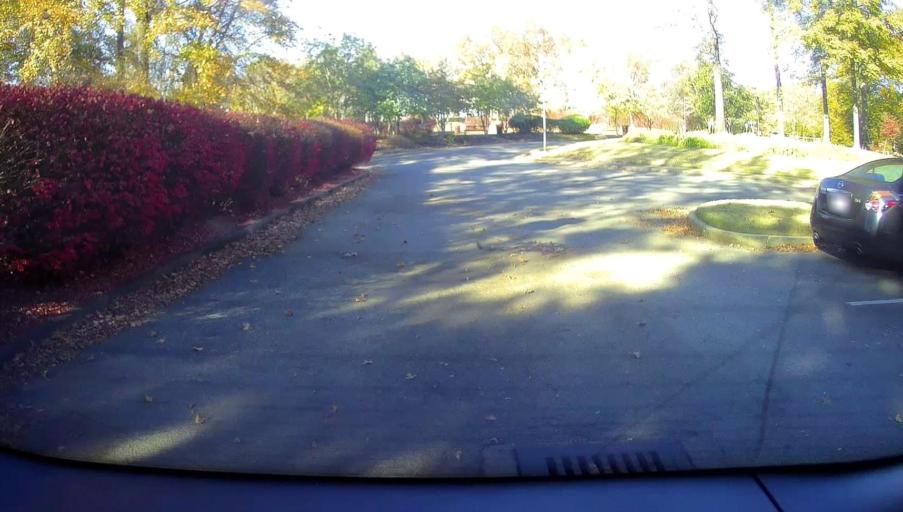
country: US
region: Tennessee
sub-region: Shelby County
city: Germantown
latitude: 35.0967
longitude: -89.8033
